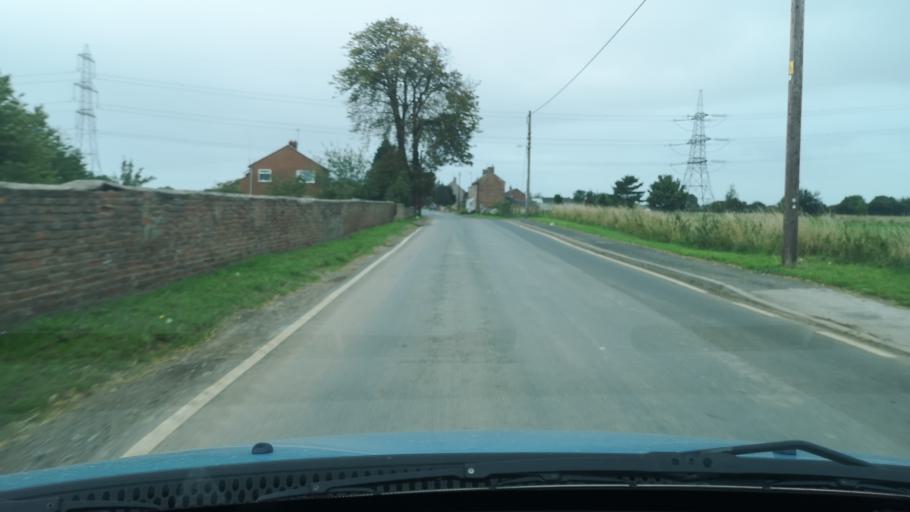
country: GB
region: England
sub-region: East Riding of Yorkshire
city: Laxton
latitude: 53.6983
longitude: -0.7419
